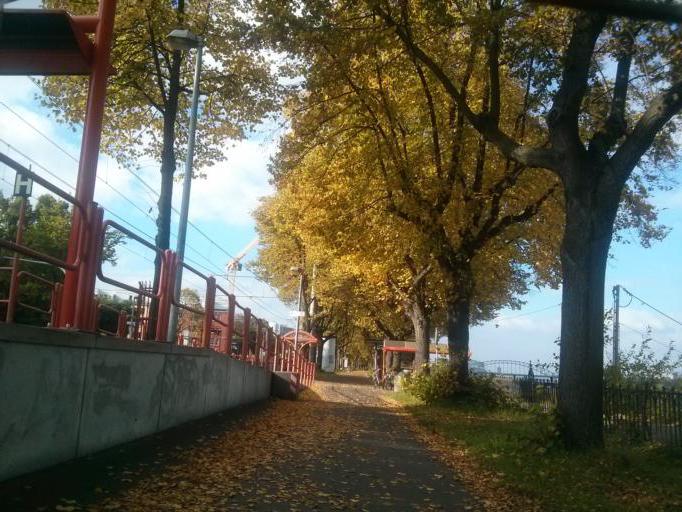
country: DE
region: North Rhine-Westphalia
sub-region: Regierungsbezirk Koln
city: Bayenthal
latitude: 50.9065
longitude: 6.9783
